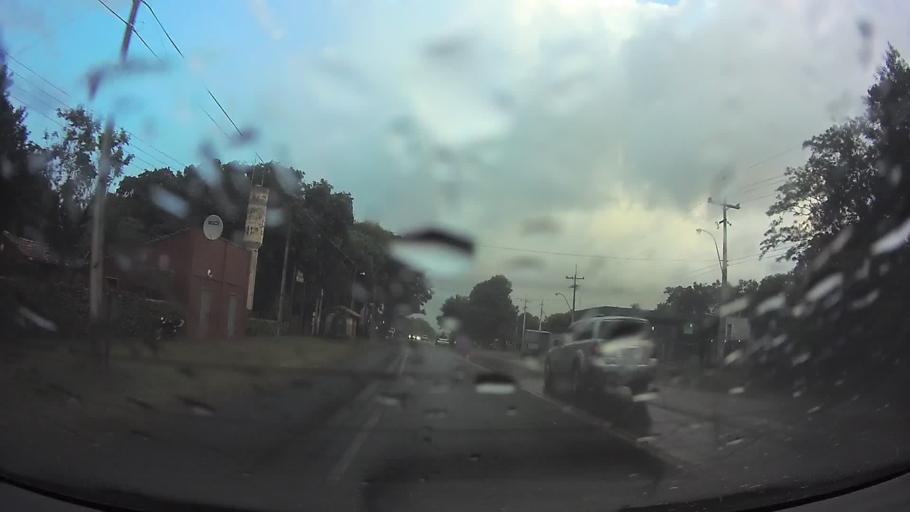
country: PY
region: Paraguari
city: Yaguaron
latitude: -25.5800
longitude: -57.2545
